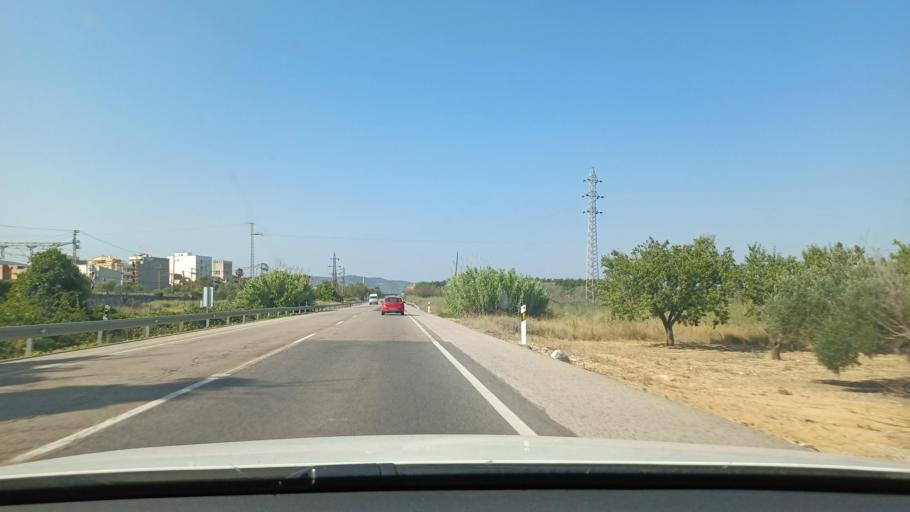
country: ES
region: Valencia
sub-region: Provincia de Castello
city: Alcala de Xivert
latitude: 40.3008
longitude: 0.2281
